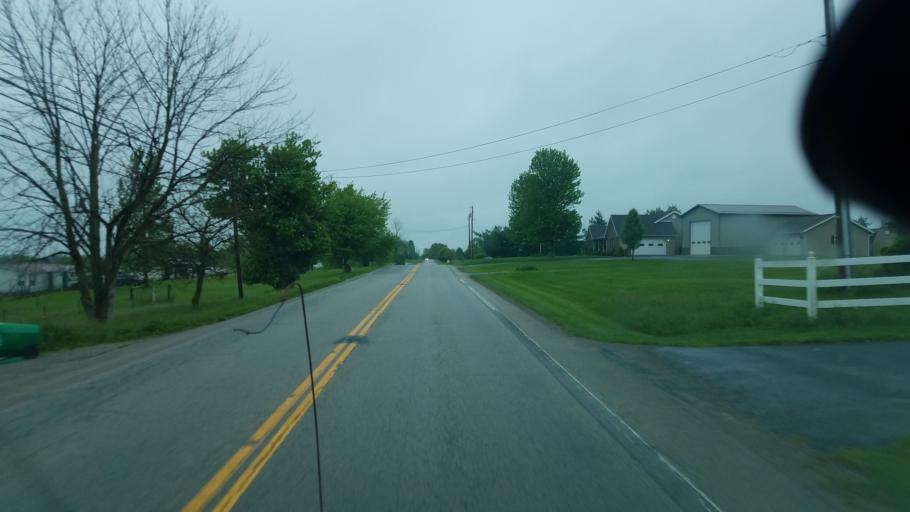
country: US
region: Ohio
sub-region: Highland County
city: Hillsboro
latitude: 39.2744
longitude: -83.5947
